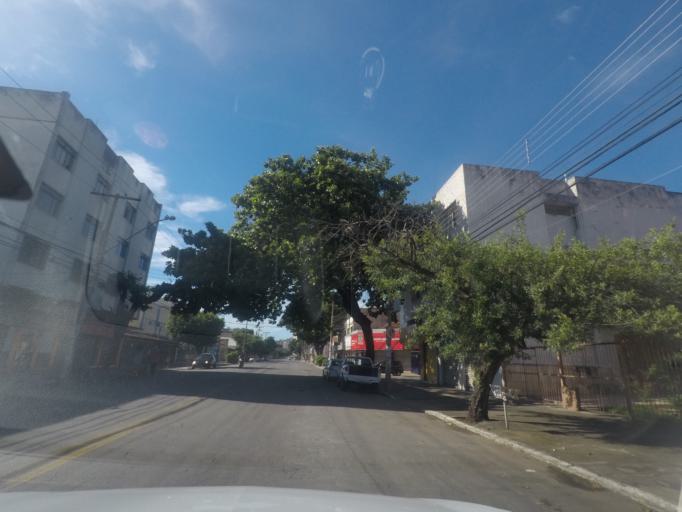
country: BR
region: Goias
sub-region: Goiania
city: Goiania
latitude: -16.6661
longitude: -49.2630
